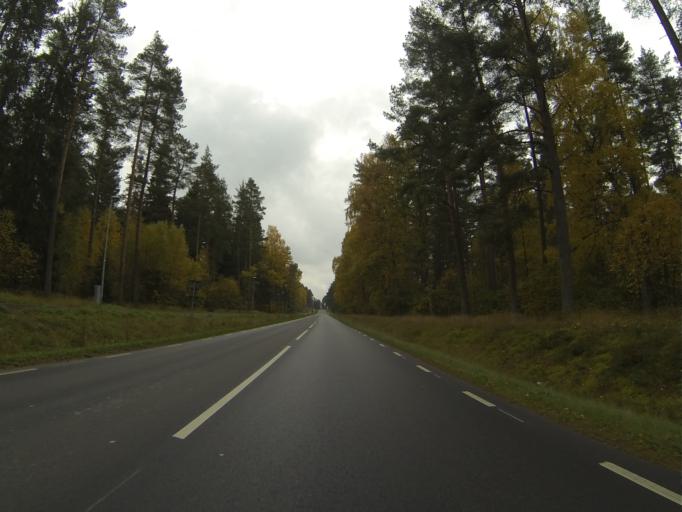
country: SE
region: Skane
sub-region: Sjobo Kommun
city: Sjoebo
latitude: 55.6363
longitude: 13.6547
